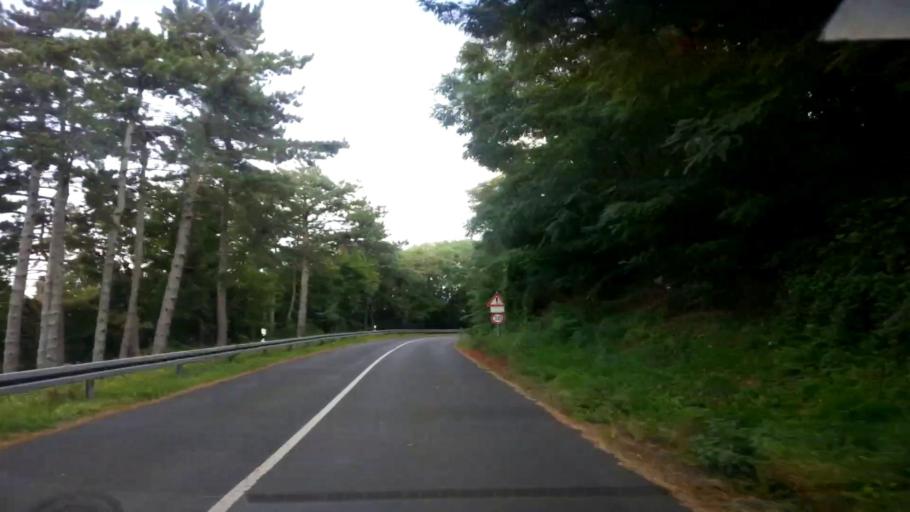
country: DE
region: Bavaria
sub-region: Regierungsbezirk Unterfranken
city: Rodelsee
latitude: 49.7279
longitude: 10.2675
